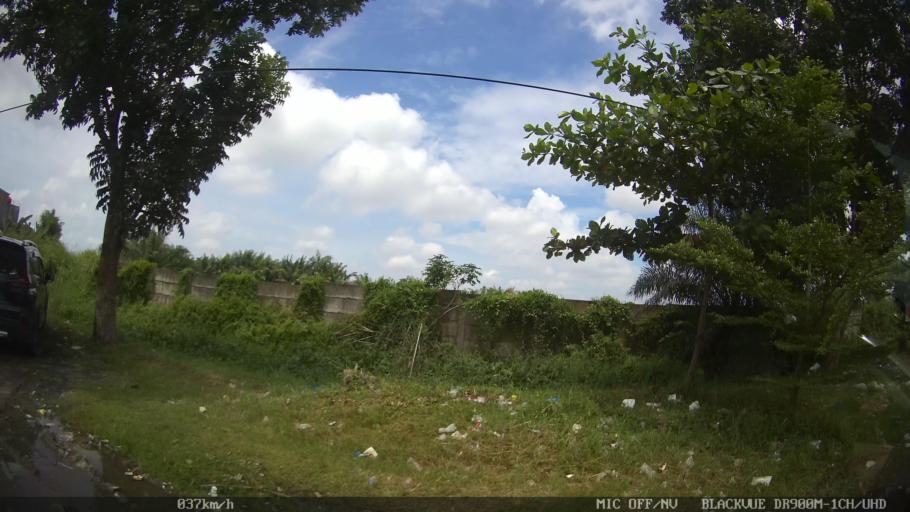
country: ID
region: North Sumatra
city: Percut
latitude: 3.6116
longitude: 98.7814
